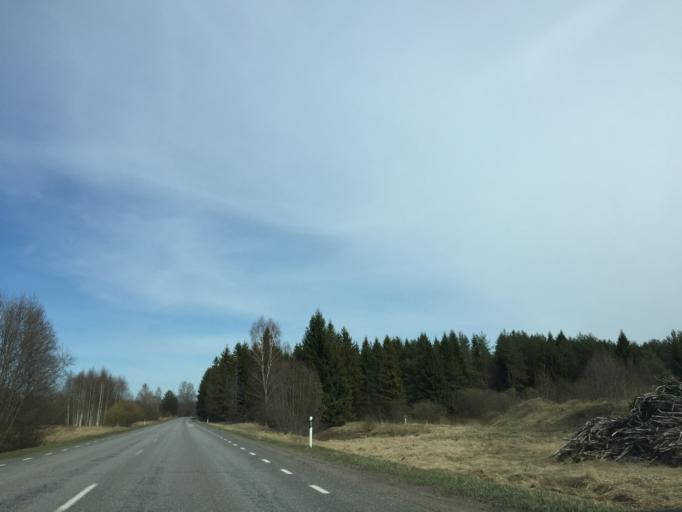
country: EE
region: Vorumaa
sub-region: Antsla vald
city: Vana-Antsla
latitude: 57.9301
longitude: 26.3453
